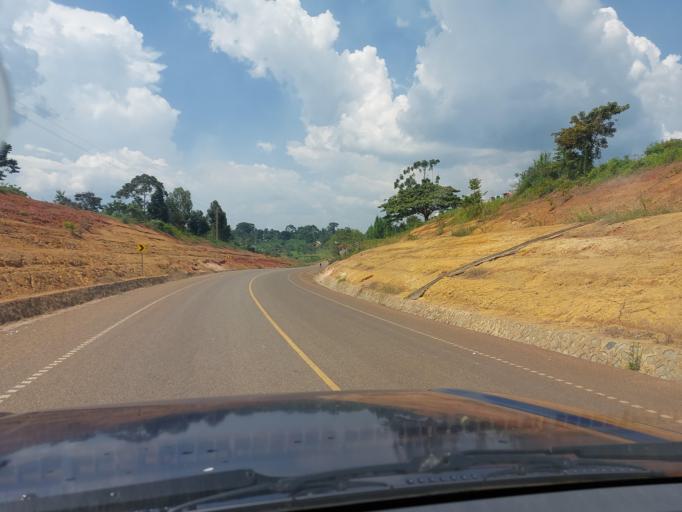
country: UG
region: Central Region
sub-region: Buikwe District
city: Buikwe
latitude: 0.3037
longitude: 33.0959
